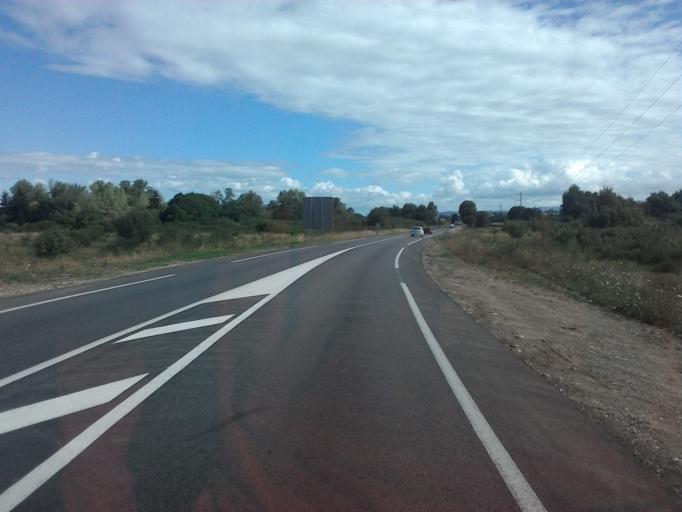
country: FR
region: Rhone-Alpes
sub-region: Departement de l'Ain
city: Ambronay
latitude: 45.9837
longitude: 5.3482
